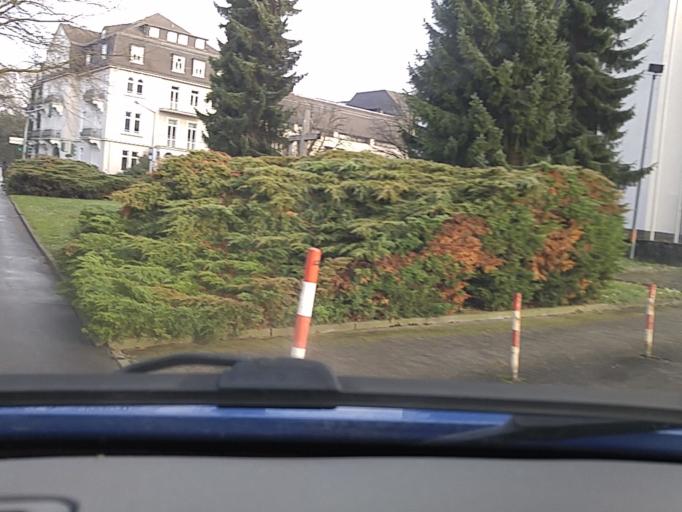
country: DE
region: Hesse
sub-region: Regierungsbezirk Darmstadt
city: Bad Nauheim
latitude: 50.3622
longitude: 8.7428
